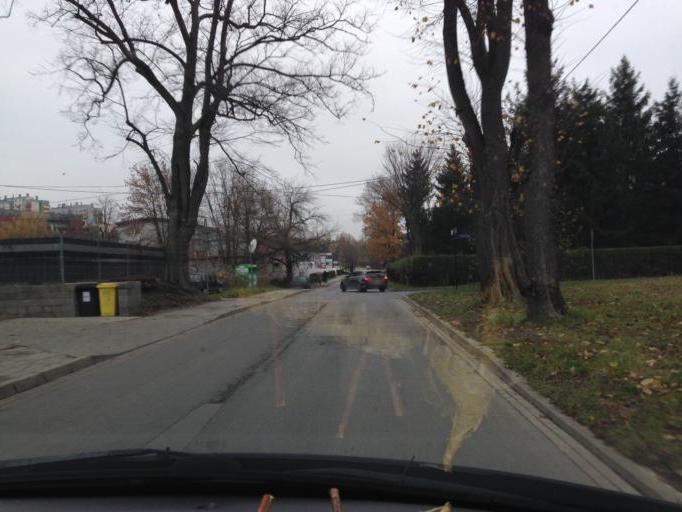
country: PL
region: Lesser Poland Voivodeship
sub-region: Powiat krakowski
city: Wrzasowice
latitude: 50.0034
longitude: 19.9567
